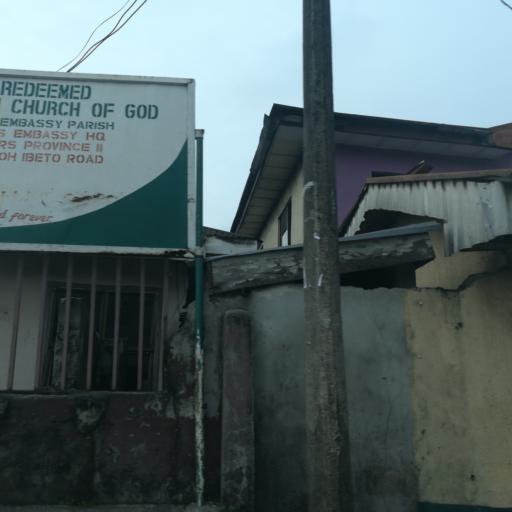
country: NG
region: Rivers
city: Port Harcourt
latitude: 4.7590
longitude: 7.0112
